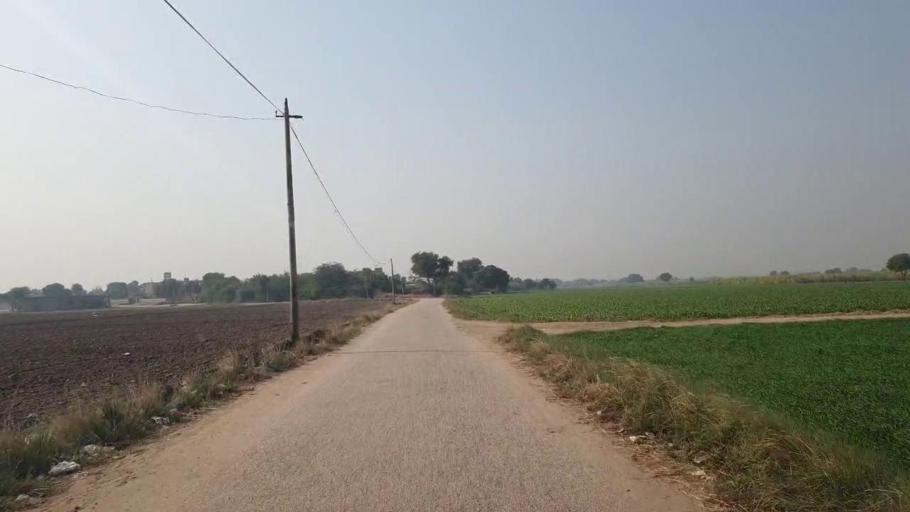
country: PK
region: Sindh
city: Kotri
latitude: 25.3587
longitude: 68.3093
